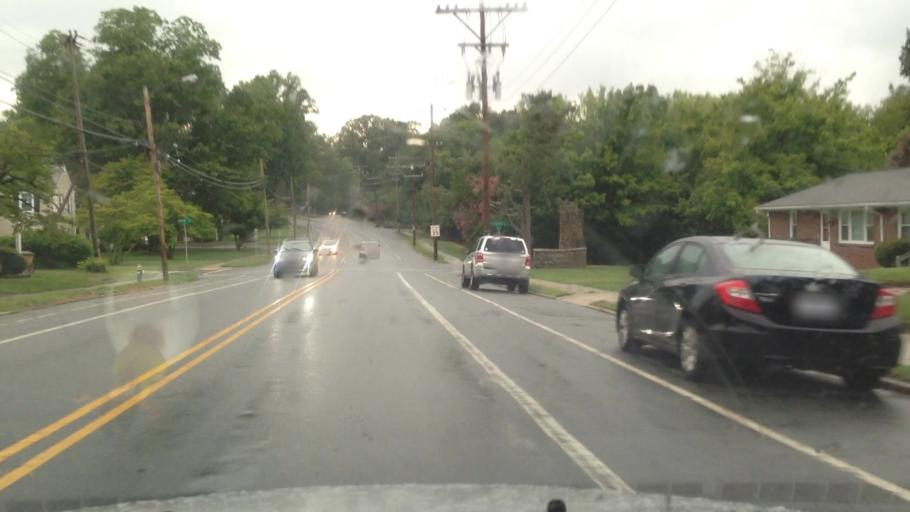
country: US
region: North Carolina
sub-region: Guilford County
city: Greensboro
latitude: 36.0641
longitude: -79.8360
